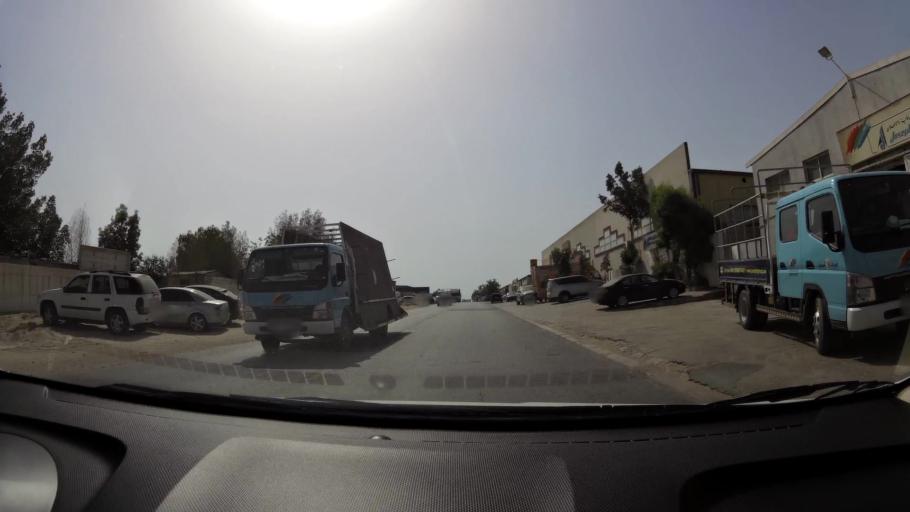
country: AE
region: Ash Shariqah
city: Sharjah
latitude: 25.2291
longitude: 55.3748
